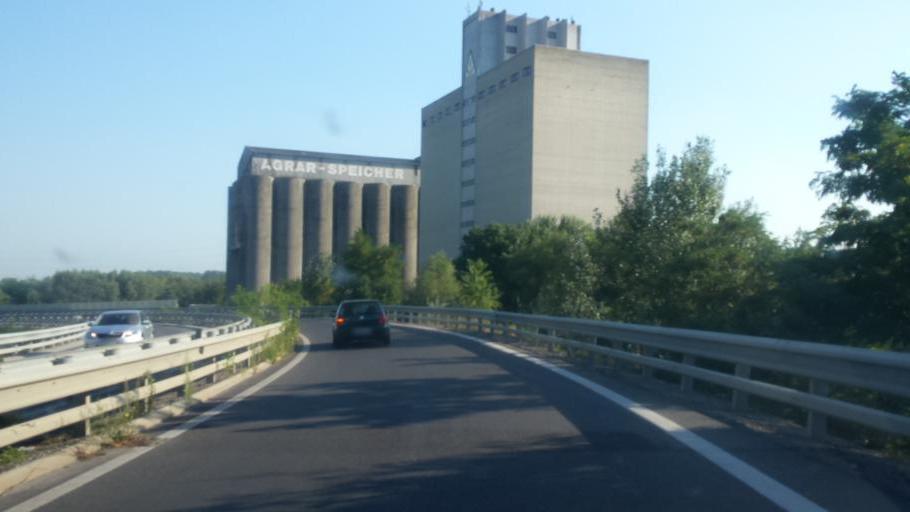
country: AT
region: Lower Austria
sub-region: Politischer Bezirk Korneuburg
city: Bisamberg
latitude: 48.3307
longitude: 16.3332
